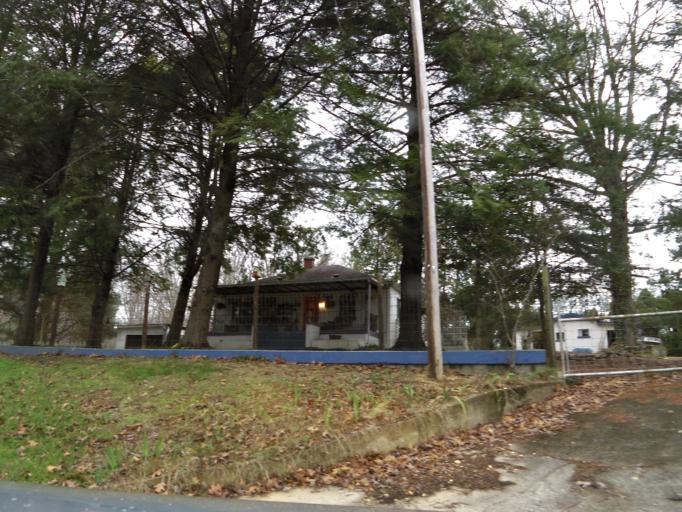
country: US
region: Tennessee
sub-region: Knox County
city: Knoxville
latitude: 35.9845
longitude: -84.0231
